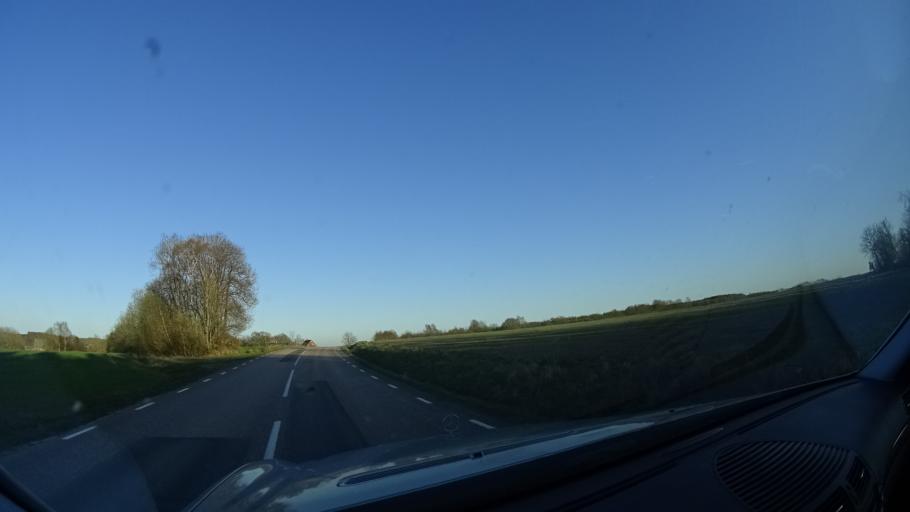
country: SE
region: Skane
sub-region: Bjuvs Kommun
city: Billesholm
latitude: 56.0282
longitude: 13.0406
